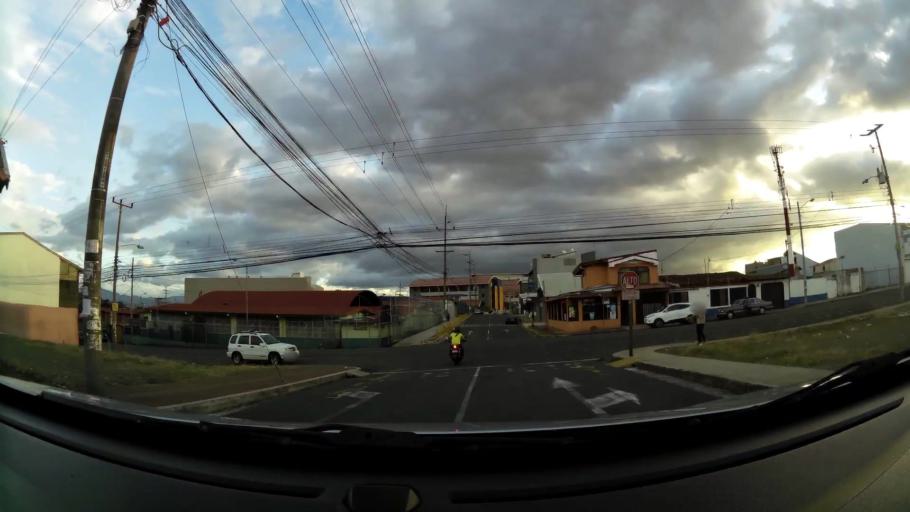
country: CR
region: Heredia
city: San Francisco
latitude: 9.9936
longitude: -84.1218
